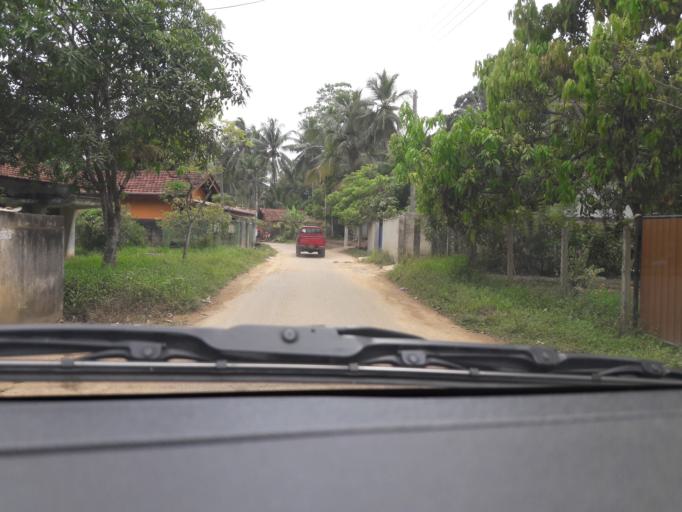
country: LK
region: Southern
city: Unawatuna
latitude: 6.0524
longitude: 80.2486
